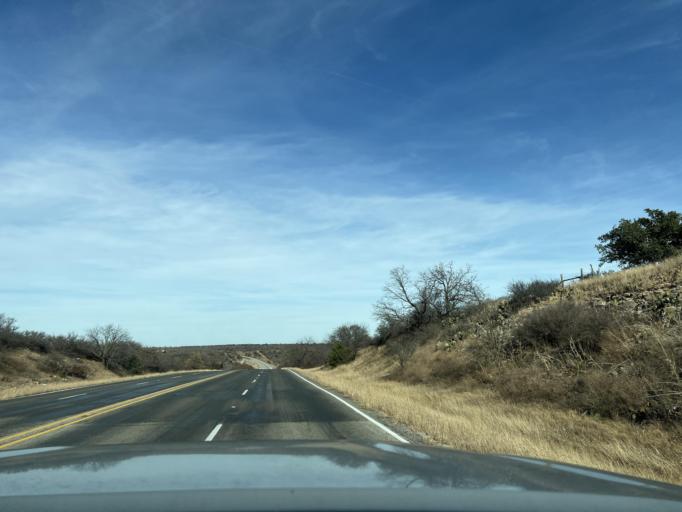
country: US
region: Texas
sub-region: Eastland County
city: Cisco
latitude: 32.4298
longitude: -98.9848
